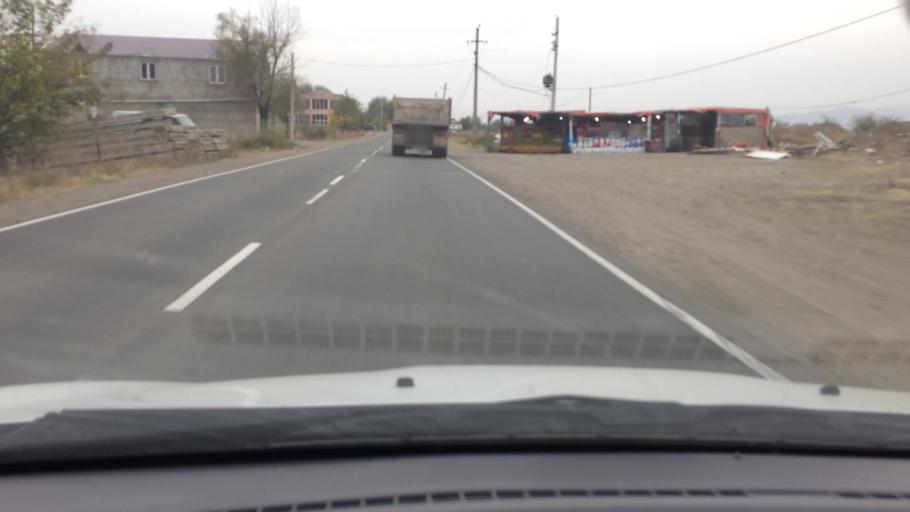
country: GE
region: Kvemo Kartli
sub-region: Marneuli
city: Marneuli
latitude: 41.4746
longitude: 44.8038
